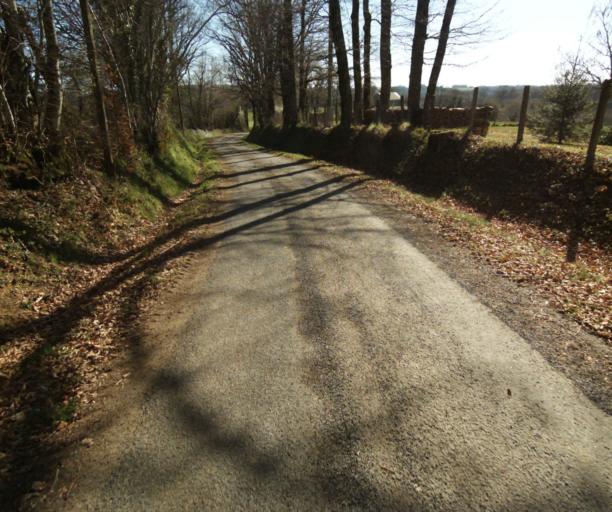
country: FR
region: Limousin
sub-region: Departement de la Correze
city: Chamboulive
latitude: 45.4305
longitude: 1.6643
